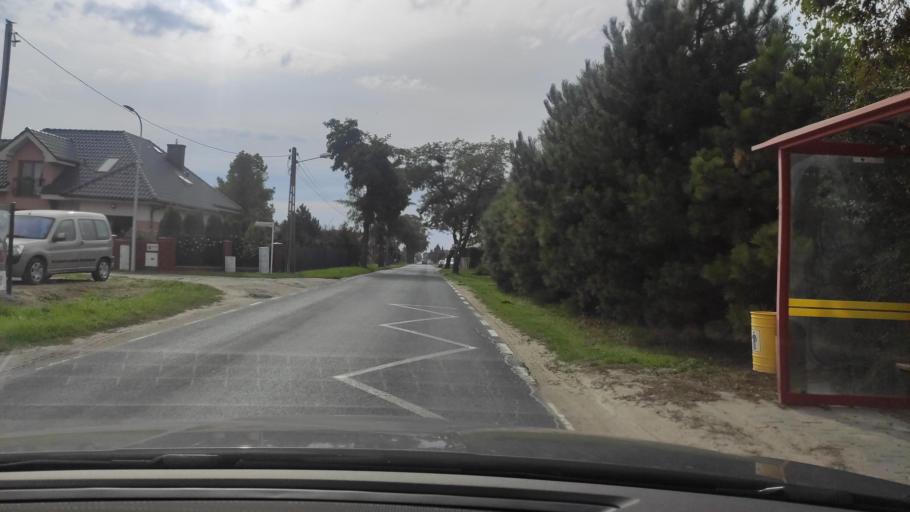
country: PL
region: Greater Poland Voivodeship
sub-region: Powiat poznanski
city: Kleszczewo
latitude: 52.3702
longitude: 17.1488
